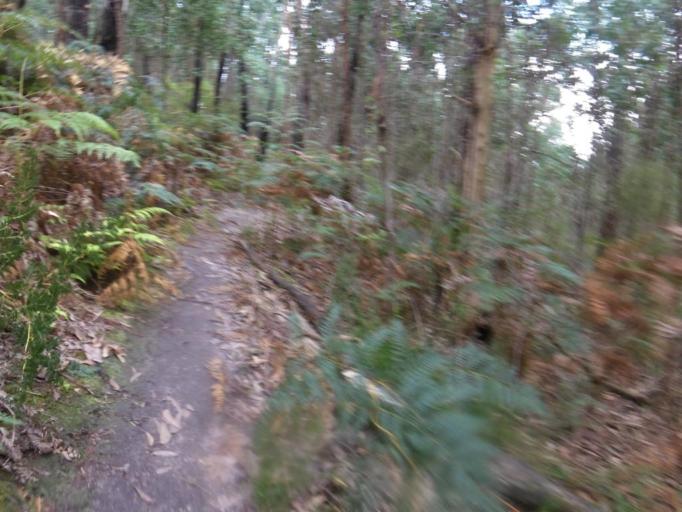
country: AU
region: Victoria
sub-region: Murrindindi
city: Kinglake West
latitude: -37.5221
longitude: 145.2466
